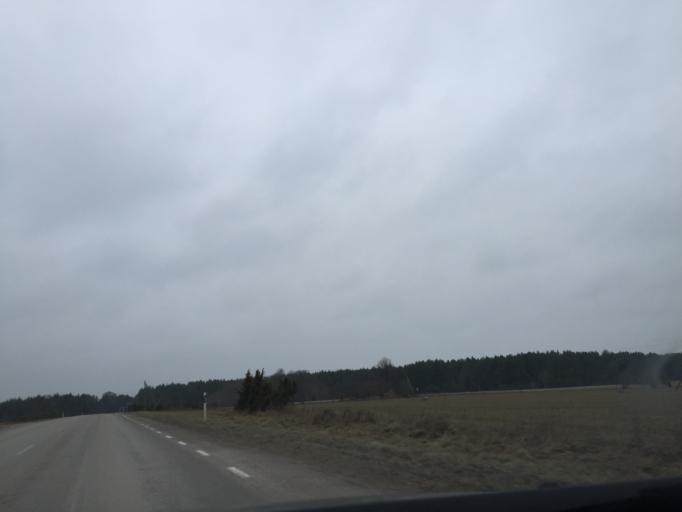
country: EE
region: Saare
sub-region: Kuressaare linn
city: Kuressaare
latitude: 58.2911
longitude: 22.2855
